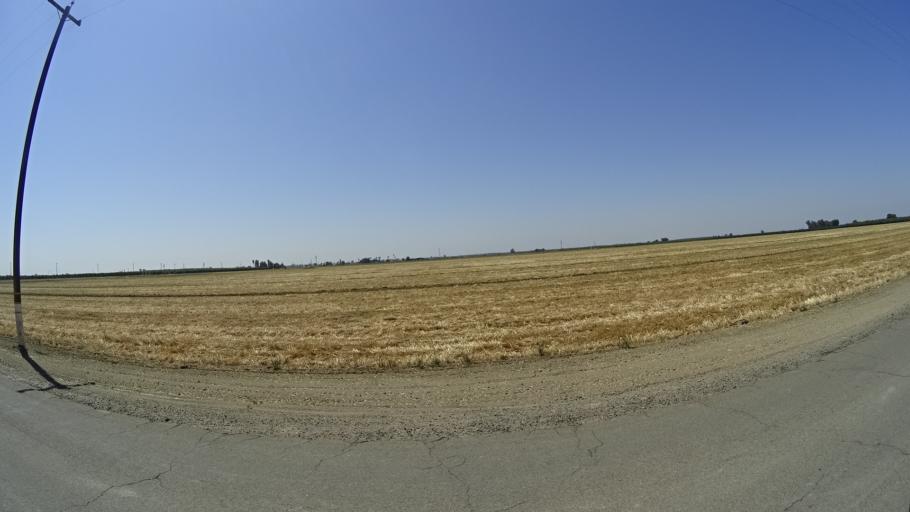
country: US
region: California
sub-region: Kings County
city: Armona
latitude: 36.3720
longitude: -119.7301
